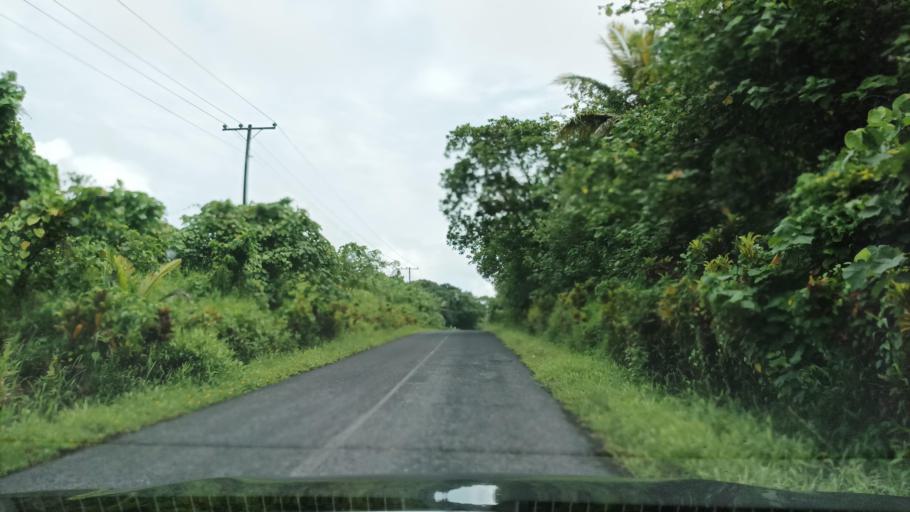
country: FM
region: Pohnpei
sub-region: Madolenihm Municipality
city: Madolenihm Municipality Government
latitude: 6.8269
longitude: 158.2989
